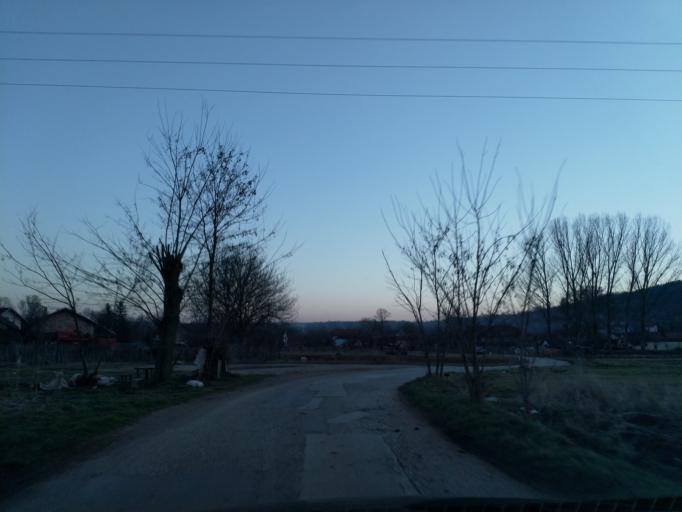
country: RS
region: Central Serbia
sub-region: Pomoravski Okrug
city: Paracin
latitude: 43.8668
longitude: 21.4752
